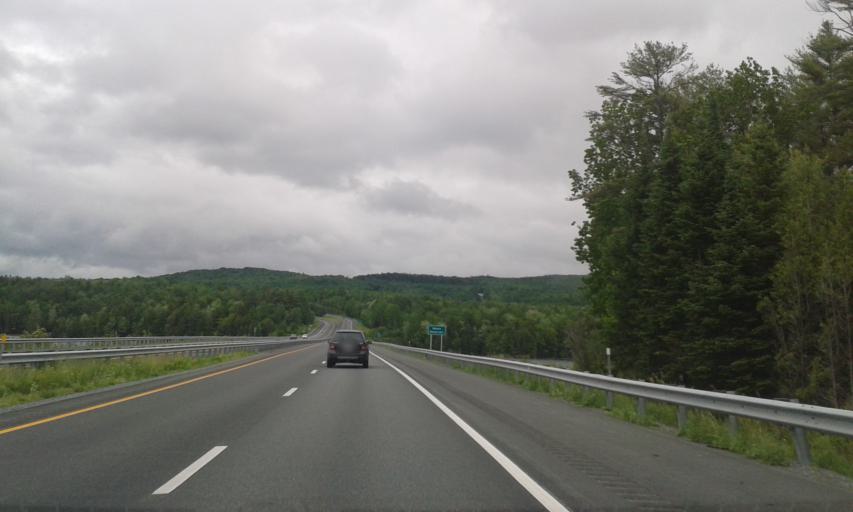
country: US
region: New Hampshire
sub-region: Grafton County
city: Littleton
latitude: 44.3170
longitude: -71.8641
